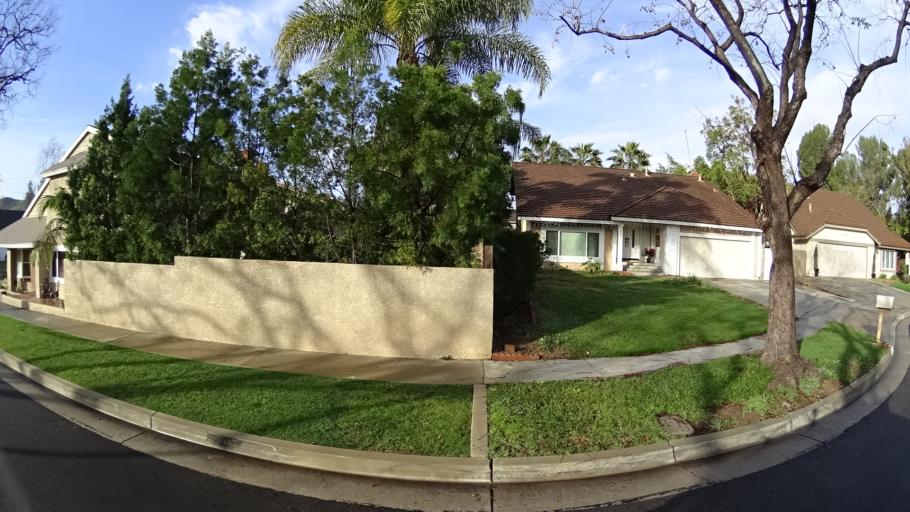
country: US
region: California
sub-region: Orange County
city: Yorba Linda
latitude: 33.8747
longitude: -117.7563
